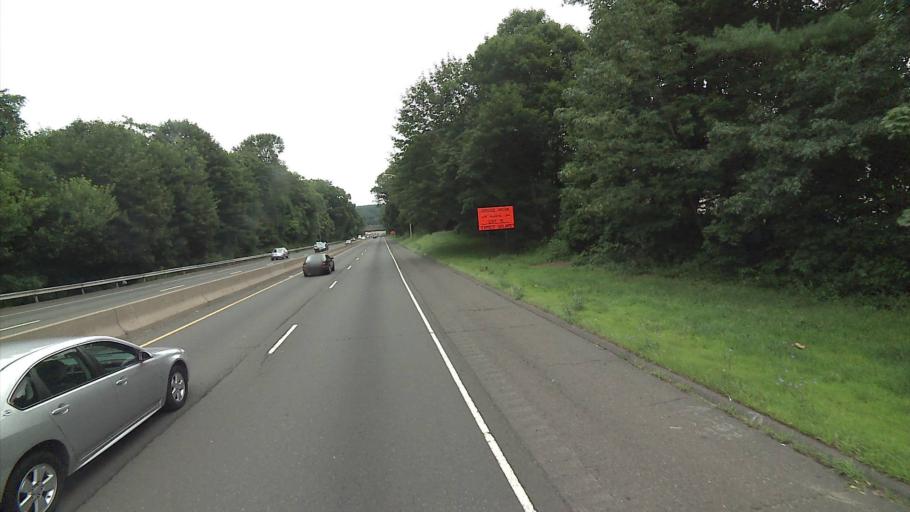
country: US
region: Connecticut
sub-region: Fairfield County
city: Shelton
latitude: 41.3096
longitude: -73.0955
